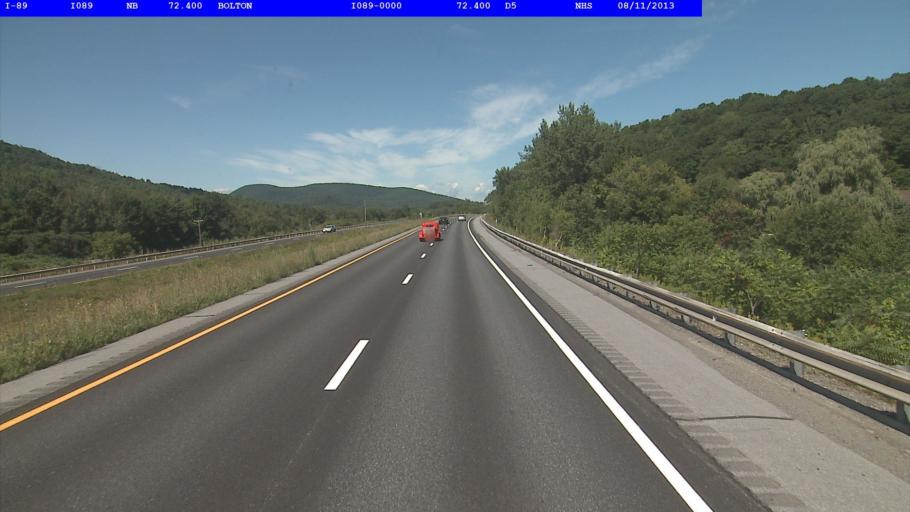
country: US
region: Vermont
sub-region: Chittenden County
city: Jericho
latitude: 44.3805
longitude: -72.9138
